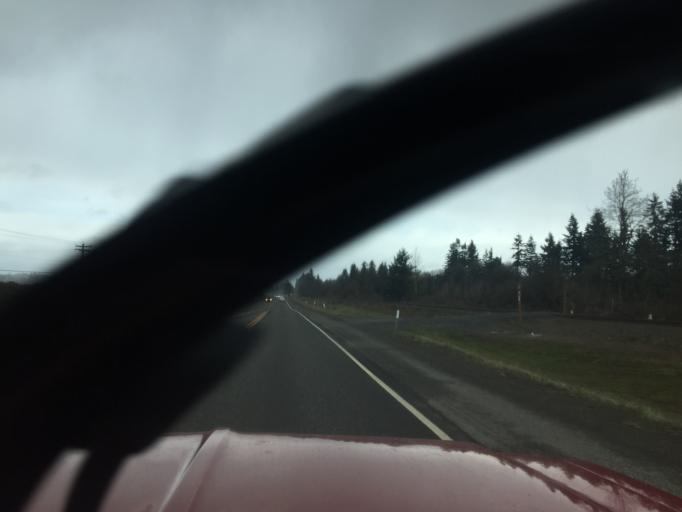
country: US
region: Oregon
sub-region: Columbia County
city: Columbia City
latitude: 45.9150
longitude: -122.8275
